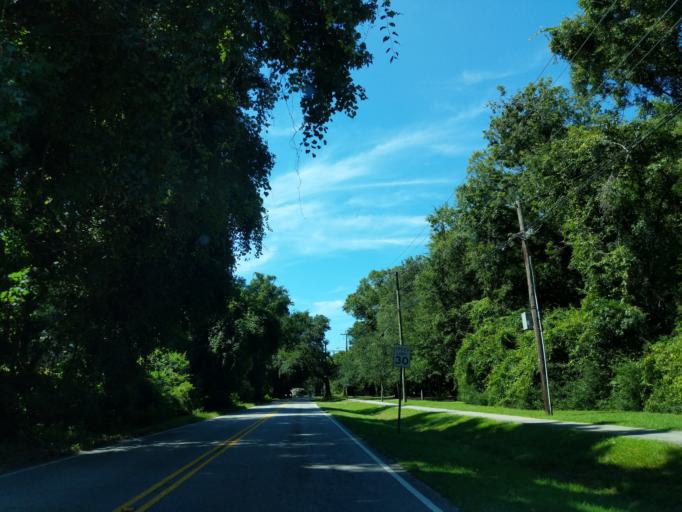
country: US
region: South Carolina
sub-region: Charleston County
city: Folly Beach
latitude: 32.7140
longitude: -79.9574
